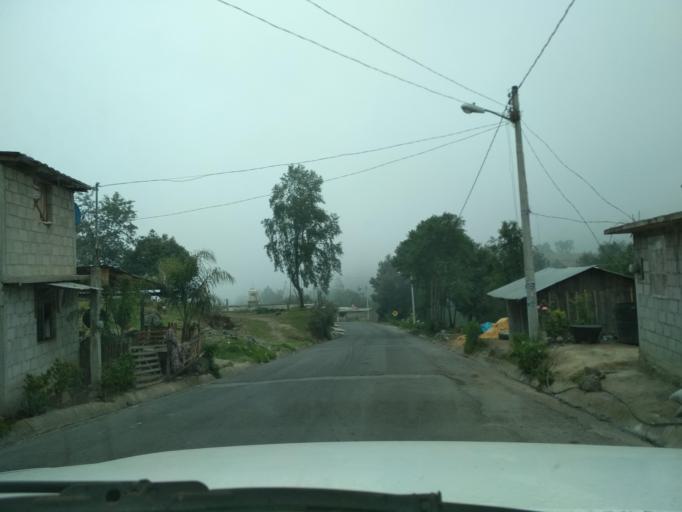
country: MX
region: Veracruz
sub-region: Mariano Escobedo
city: San Isidro el Berro
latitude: 18.9475
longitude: -97.2013
